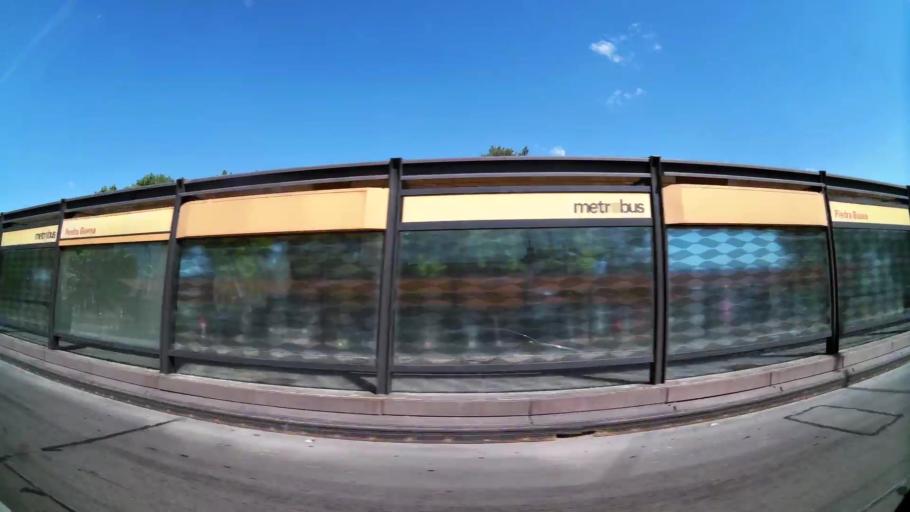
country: AR
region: Buenos Aires F.D.
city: Villa Lugano
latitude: -34.6948
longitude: -58.4666
